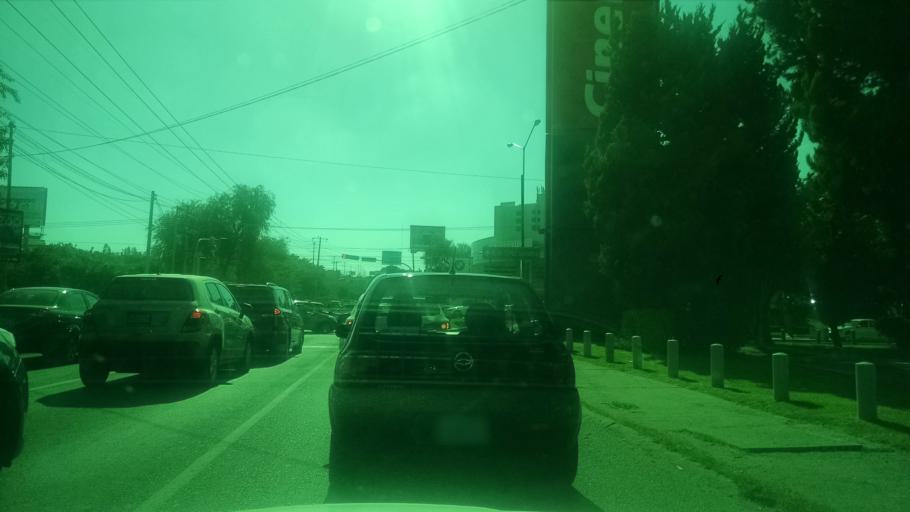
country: MX
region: Guanajuato
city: Leon
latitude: 21.1548
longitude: -101.6965
